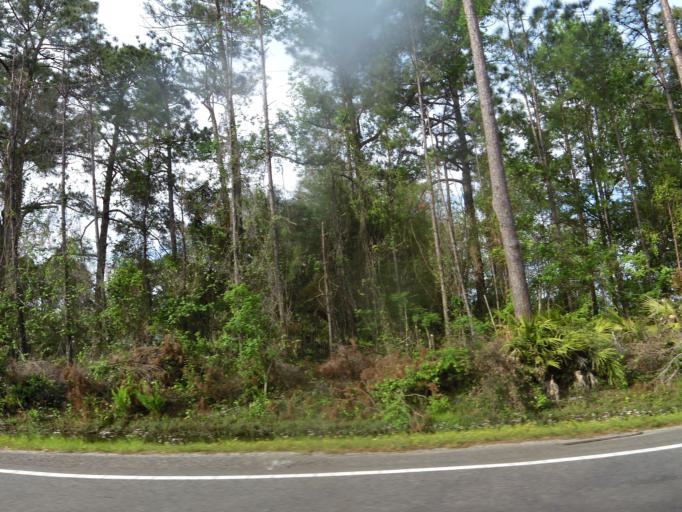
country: US
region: Florida
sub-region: Nassau County
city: Yulee
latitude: 30.6863
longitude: -81.6586
